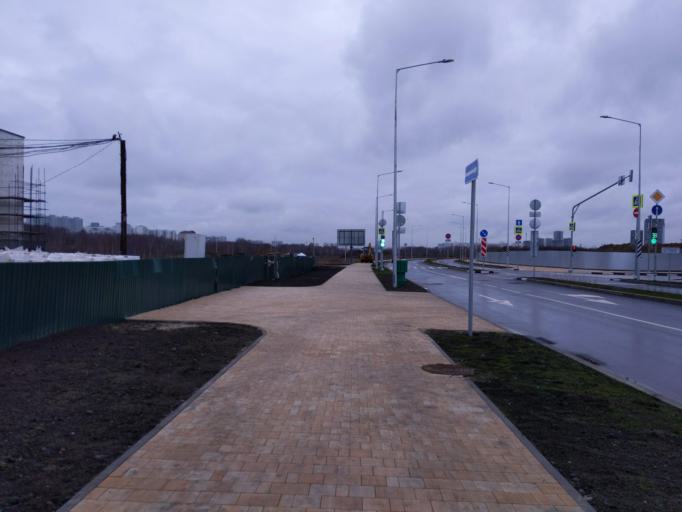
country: RU
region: Moscow
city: Strogino
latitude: 55.8133
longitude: 37.4222
